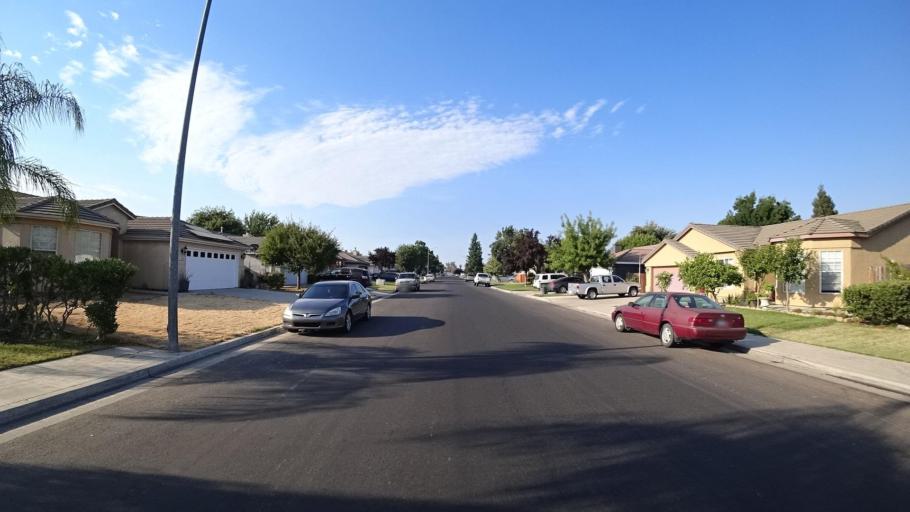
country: US
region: California
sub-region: Fresno County
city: Sunnyside
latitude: 36.7144
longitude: -119.6938
